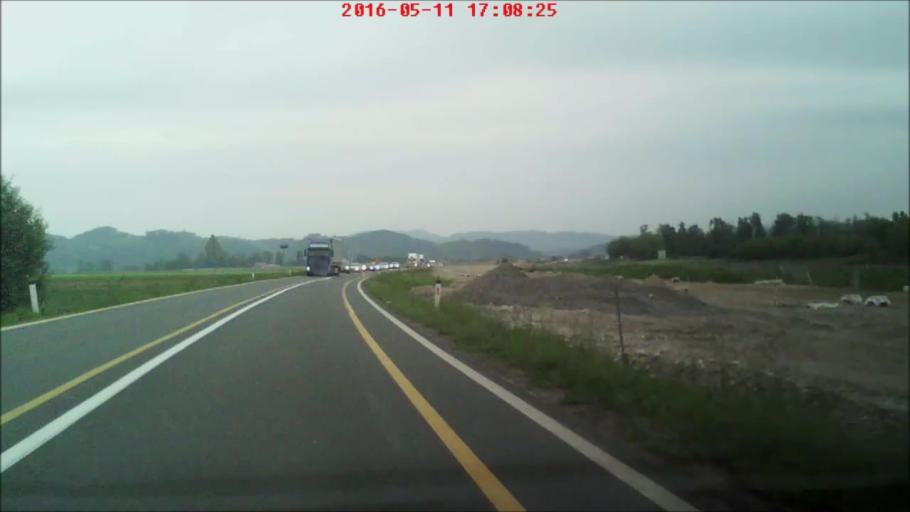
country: SI
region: Hajdina
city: Spodnja Hajdina
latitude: 46.3849
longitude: 15.8637
